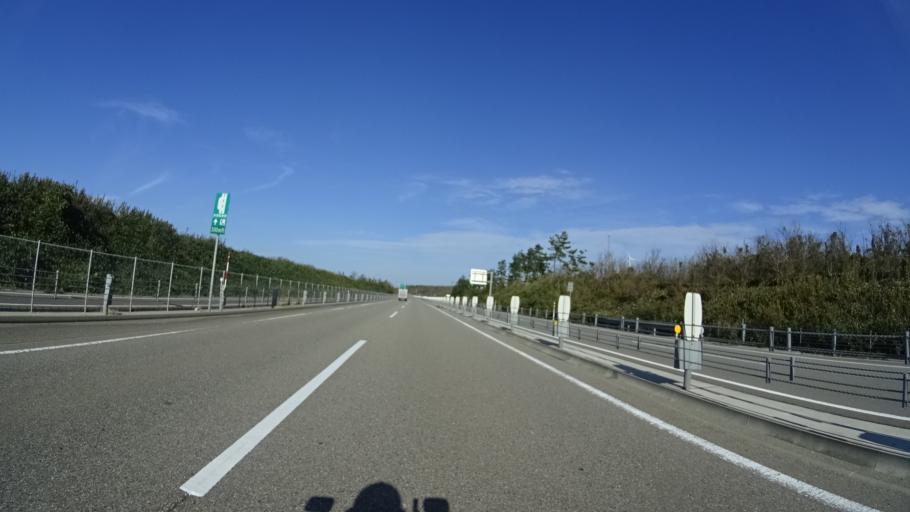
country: JP
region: Ishikawa
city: Kanazawa-shi
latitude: 36.6600
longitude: 136.6423
